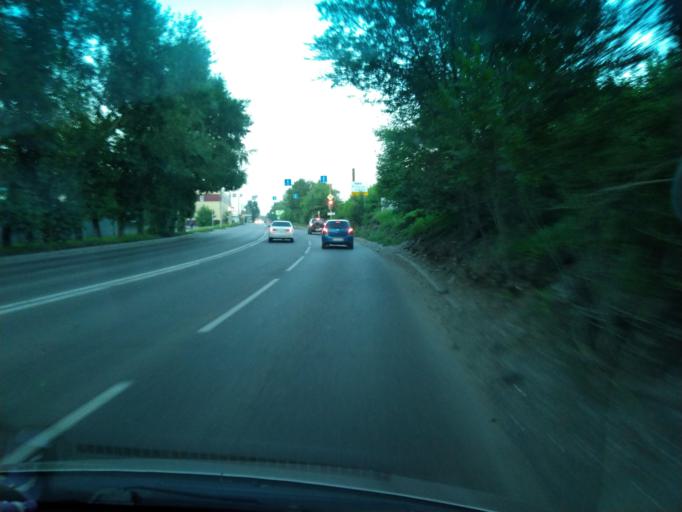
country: RU
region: Krasnoyarskiy
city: Krasnoyarsk
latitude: 55.9890
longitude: 92.9083
